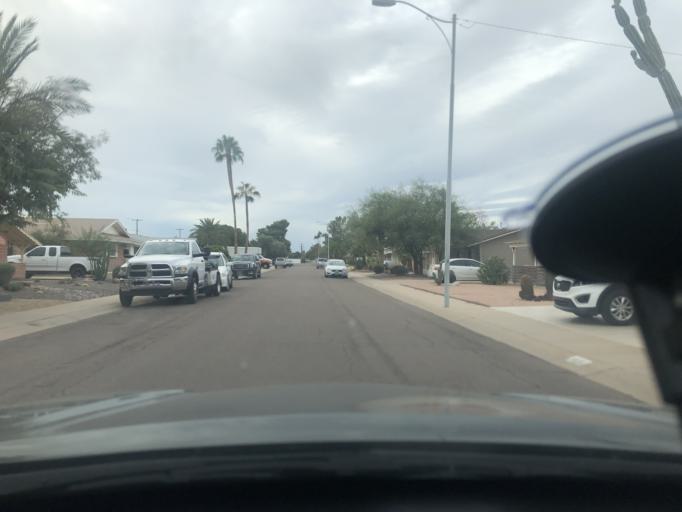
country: US
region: Arizona
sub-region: Maricopa County
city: Scottsdale
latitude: 33.4796
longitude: -111.8974
